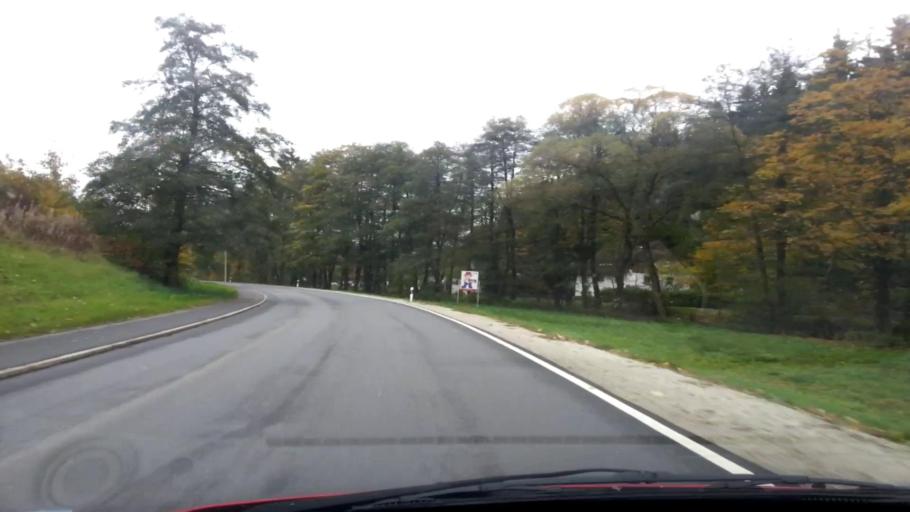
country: DE
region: Bavaria
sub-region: Upper Franconia
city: Warmensteinach
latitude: 49.9874
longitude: 11.7729
